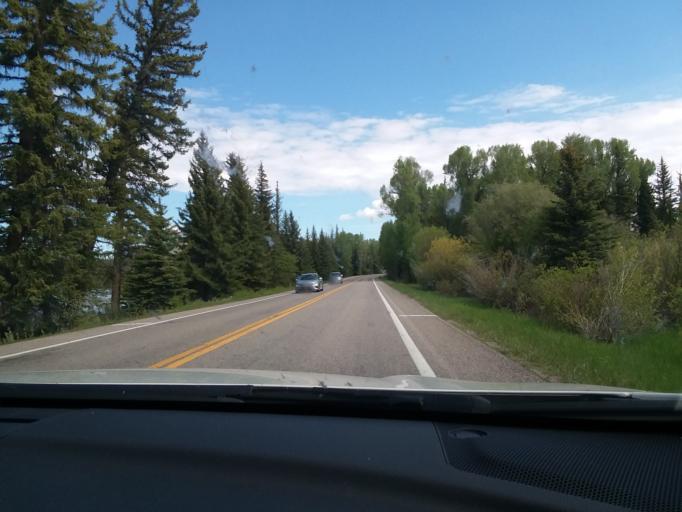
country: US
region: Wyoming
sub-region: Teton County
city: Jackson
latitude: 43.8345
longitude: -110.5133
